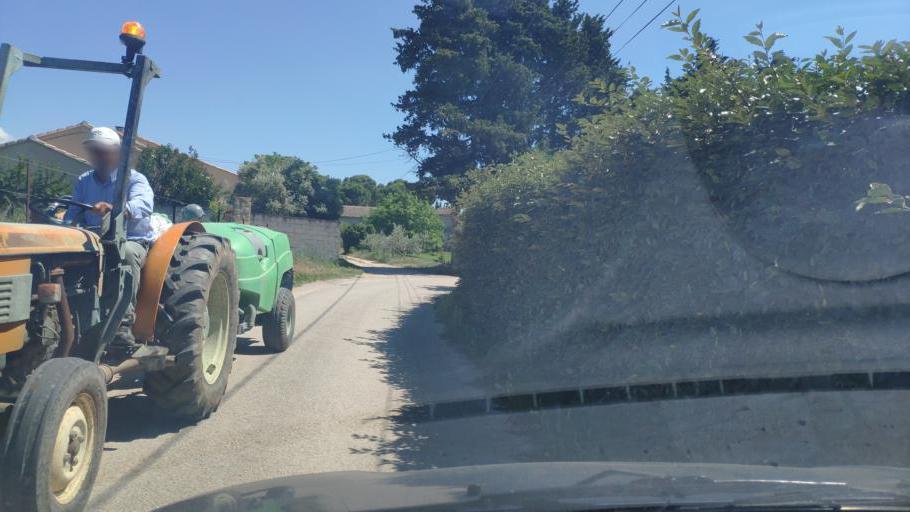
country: FR
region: Provence-Alpes-Cote d'Azur
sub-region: Departement du Vaucluse
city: Carpentras
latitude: 44.0796
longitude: 5.0557
